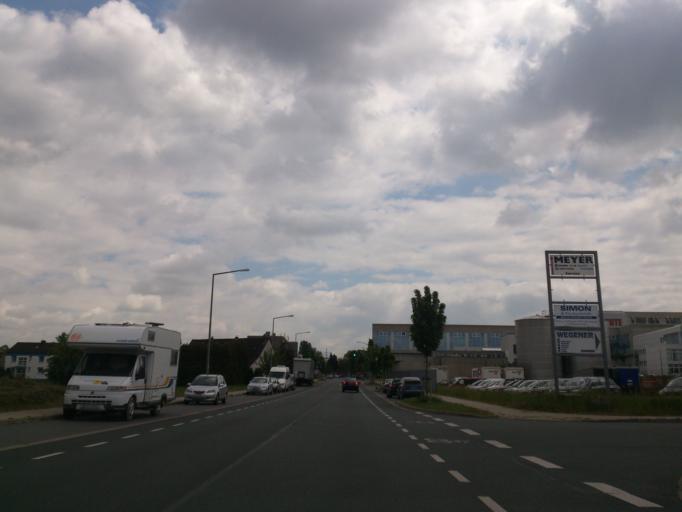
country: DE
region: North Rhine-Westphalia
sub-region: Regierungsbezirk Detmold
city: Paderborn
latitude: 51.7053
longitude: 8.7328
